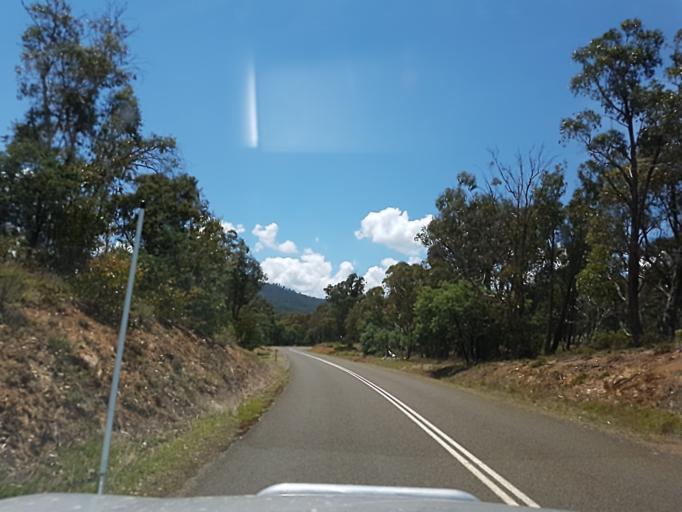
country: AU
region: Victoria
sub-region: Alpine
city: Mount Beauty
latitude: -36.9337
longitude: 147.7818
